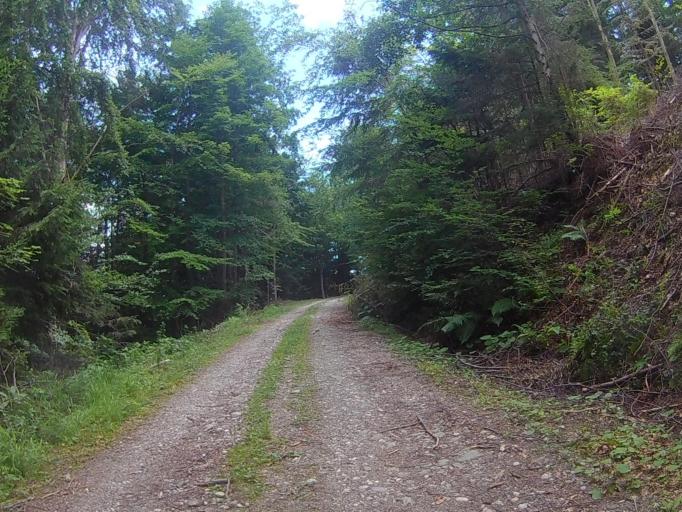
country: SI
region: Selnica ob Dravi
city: Selnica ob Dravi
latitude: 46.5170
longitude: 15.4747
